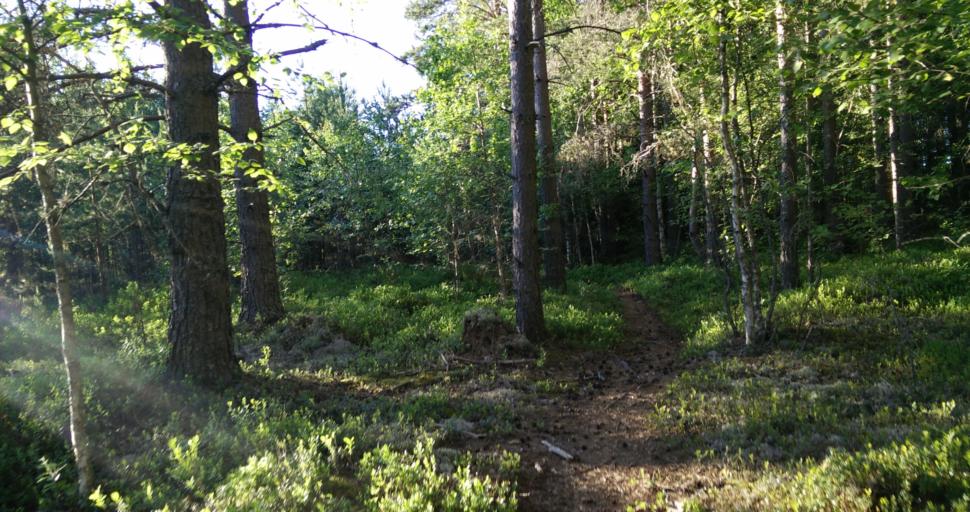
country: SE
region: Vaermland
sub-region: Hagfors Kommun
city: Hagfors
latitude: 60.0202
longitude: 13.5830
